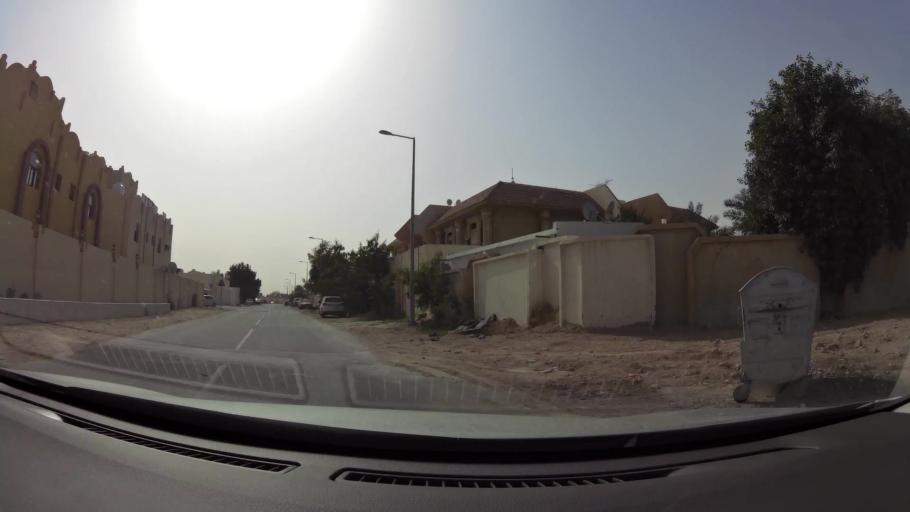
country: QA
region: Baladiyat ar Rayyan
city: Ar Rayyan
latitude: 25.2478
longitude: 51.4404
